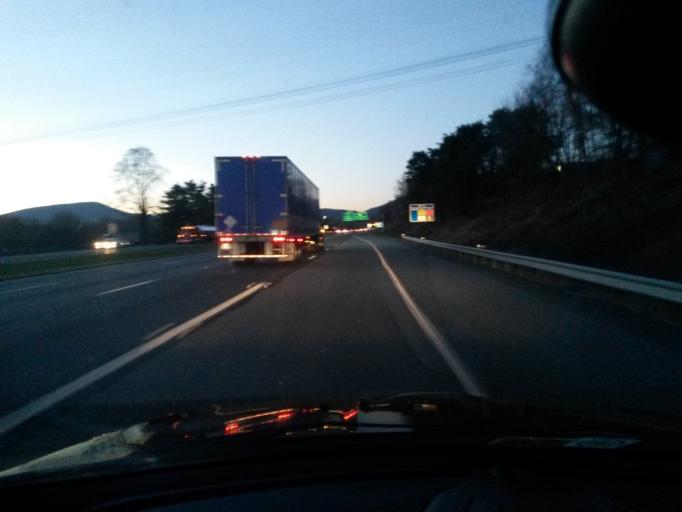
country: US
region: Virginia
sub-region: Roanoke County
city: Hollins
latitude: 37.3113
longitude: -79.9762
